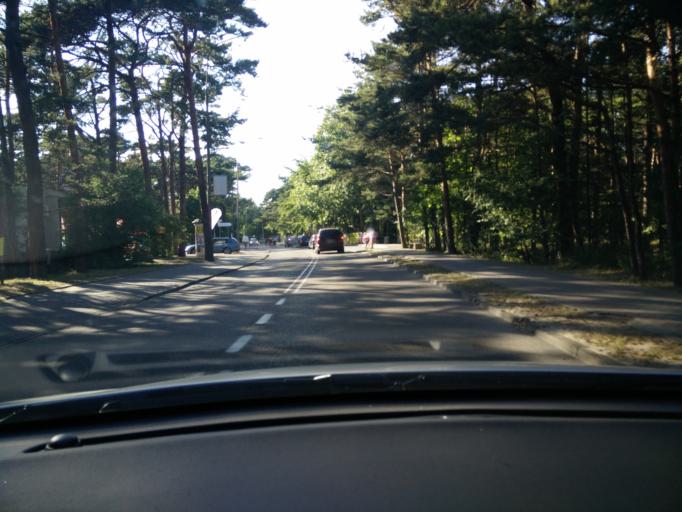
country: PL
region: Pomeranian Voivodeship
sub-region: Powiat pucki
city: Jastarnia
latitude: 54.6796
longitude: 18.7204
